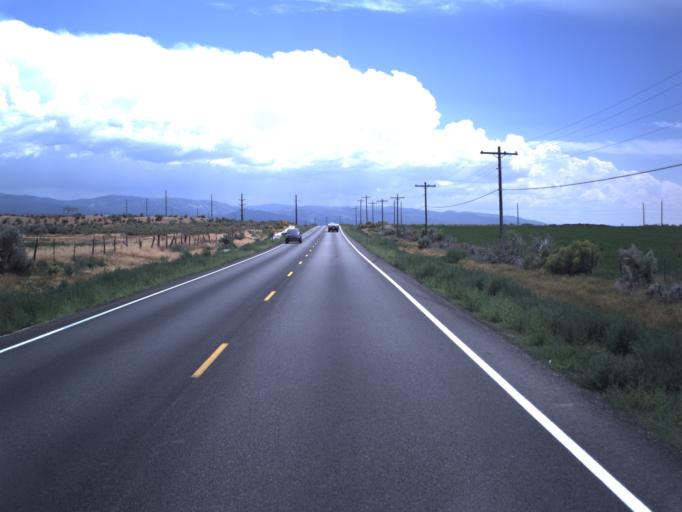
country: US
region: Utah
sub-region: Sanpete County
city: Moroni
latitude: 39.5551
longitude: -111.6005
